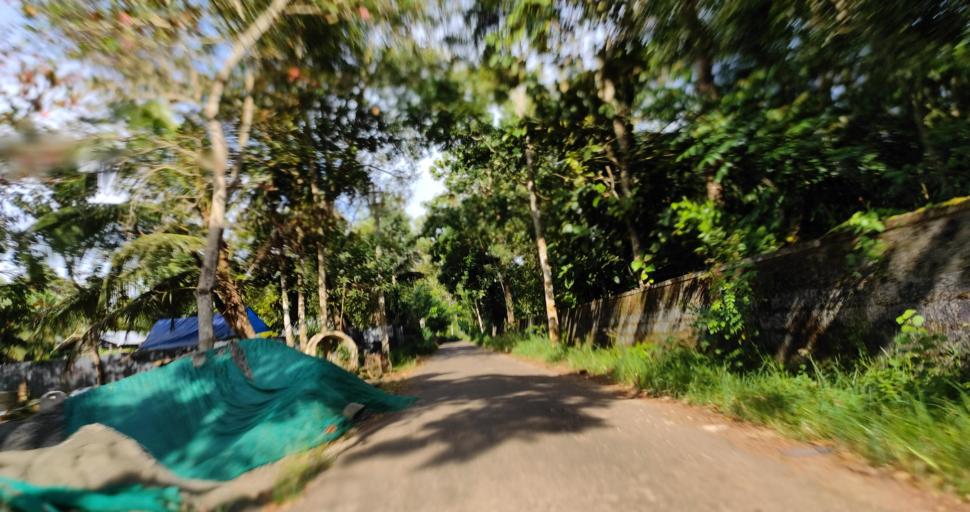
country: IN
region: Kerala
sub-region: Alappuzha
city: Shertallai
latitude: 9.6010
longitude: 76.3323
